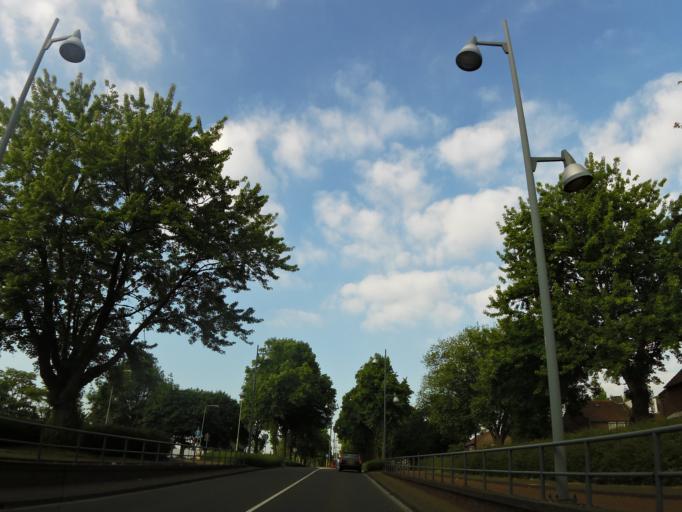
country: NL
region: Limburg
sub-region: Gemeente Sittard-Geleen
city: Sittard
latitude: 50.9883
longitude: 5.8513
